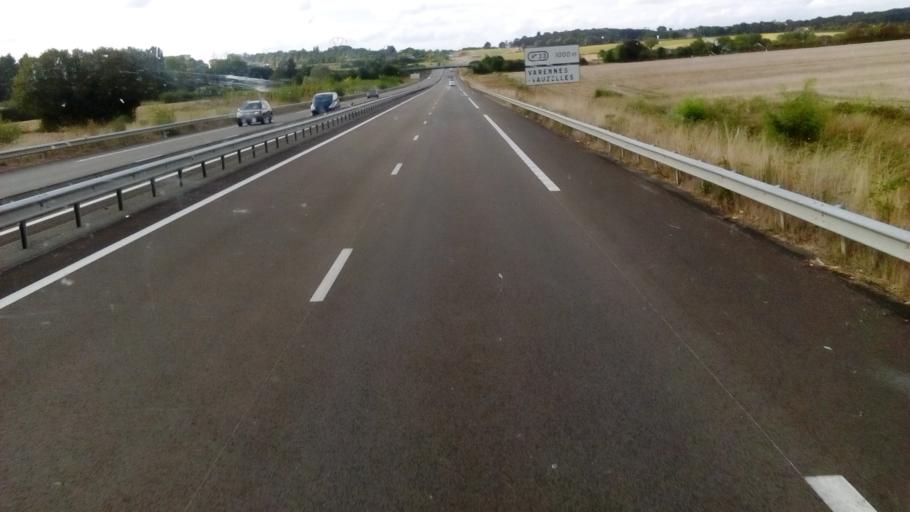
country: FR
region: Bourgogne
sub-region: Departement de la Nievre
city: Varennes-Vauzelles
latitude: 47.0286
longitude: 3.1637
